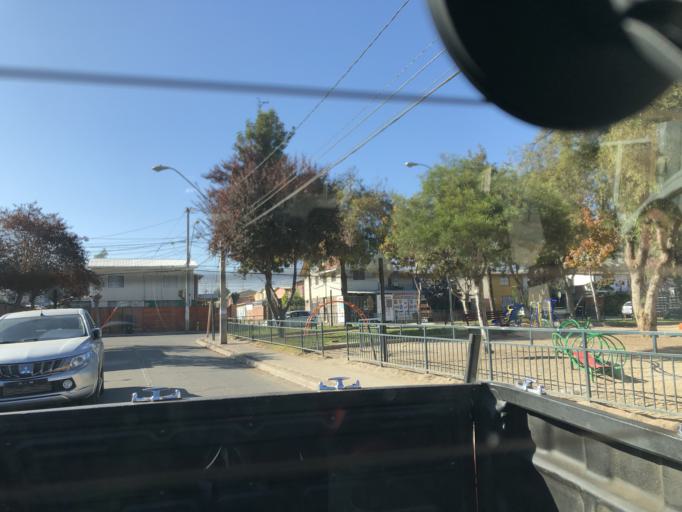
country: CL
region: Santiago Metropolitan
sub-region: Provincia de Cordillera
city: Puente Alto
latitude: -33.5955
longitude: -70.5693
